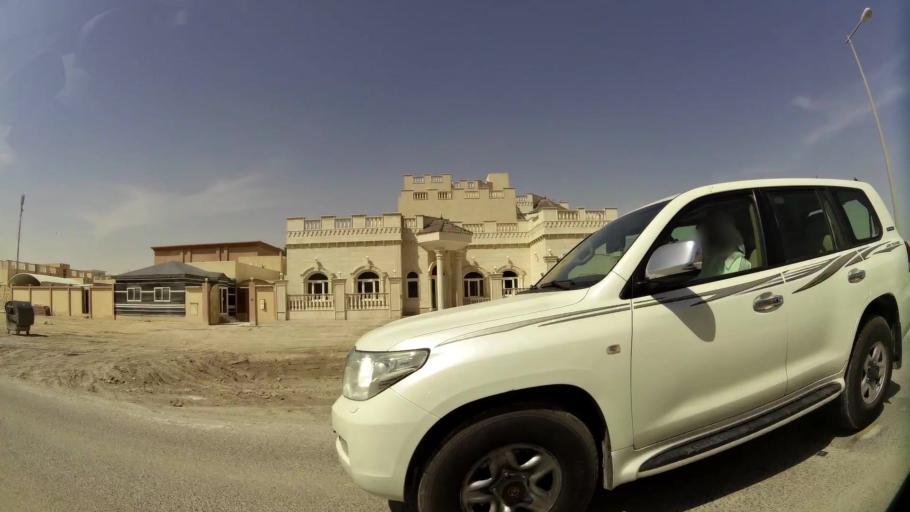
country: QA
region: Baladiyat ar Rayyan
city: Ar Rayyan
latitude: 25.2482
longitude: 51.4004
